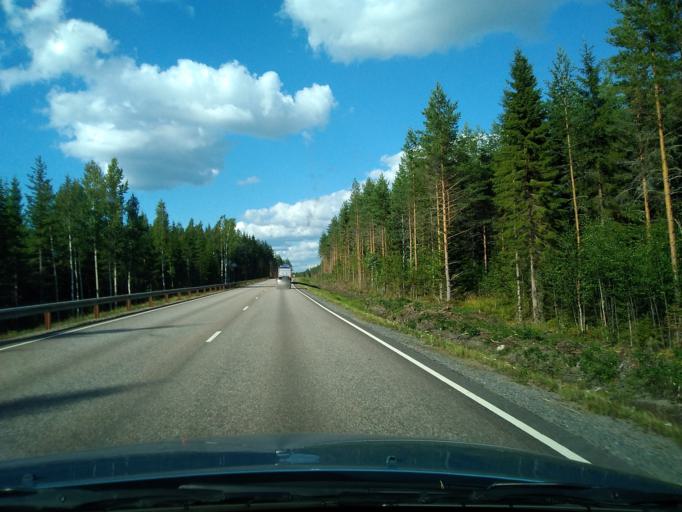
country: FI
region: Central Finland
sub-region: Keuruu
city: Keuruu
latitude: 62.1433
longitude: 24.7452
